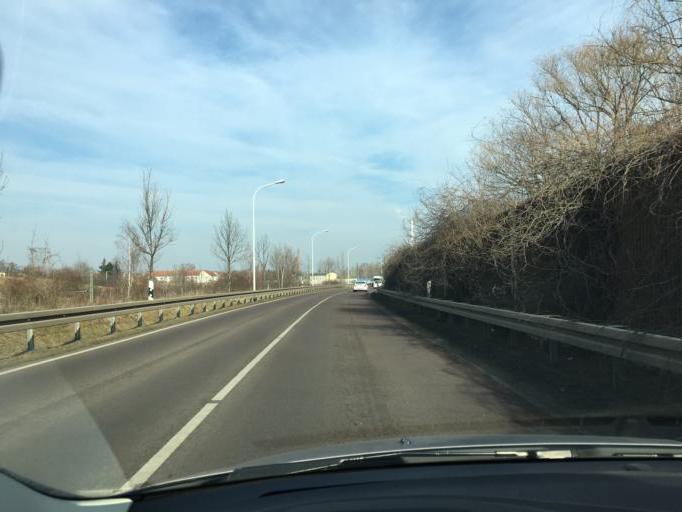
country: DE
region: Saxony-Anhalt
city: Schkopau
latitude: 51.4449
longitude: 11.9892
